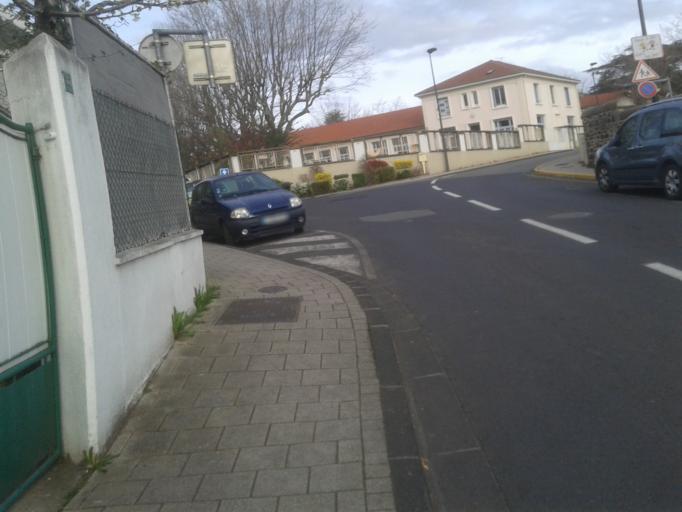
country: FR
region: Auvergne
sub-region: Departement du Puy-de-Dome
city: Chamalieres
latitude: 45.7692
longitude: 3.0696
